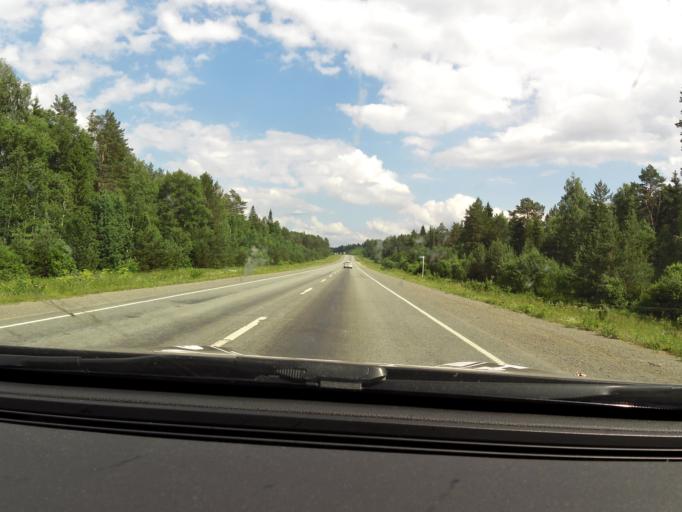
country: RU
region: Sverdlovsk
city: Bisert'
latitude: 56.8293
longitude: 58.9686
